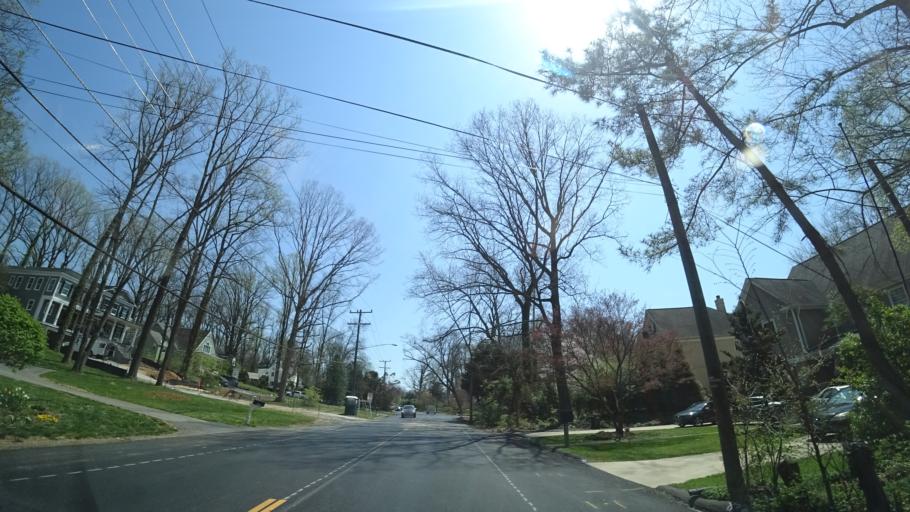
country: US
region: Maryland
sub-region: Montgomery County
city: Bethesda
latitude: 38.9908
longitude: -77.1174
